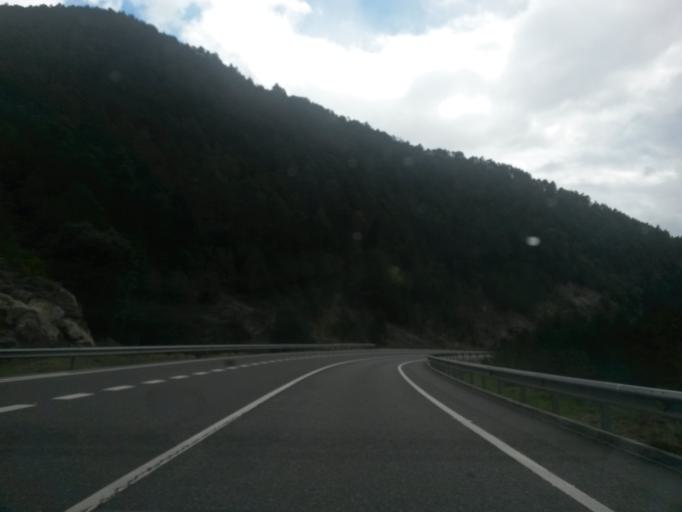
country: ES
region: Catalonia
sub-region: Provincia de Barcelona
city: Baga
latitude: 42.2713
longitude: 1.8544
